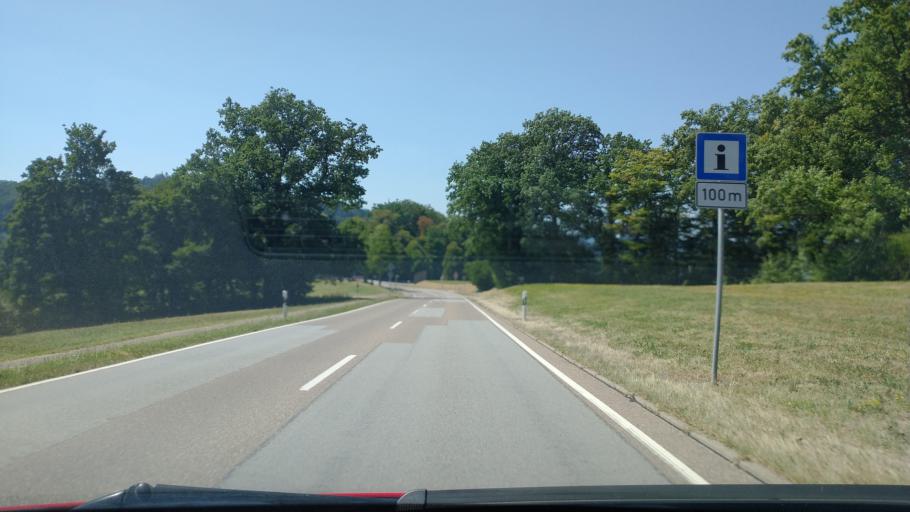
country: DE
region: Baden-Wuerttemberg
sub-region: Regierungsbezirk Stuttgart
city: Lorch
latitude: 48.8011
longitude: 9.7076
